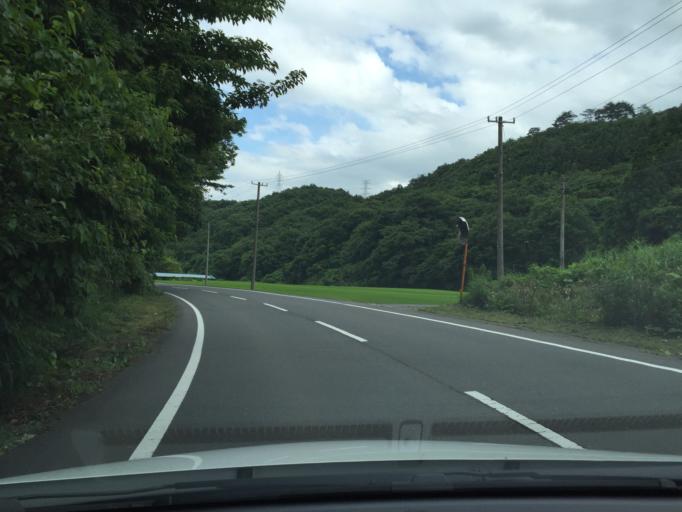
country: JP
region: Fukushima
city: Sukagawa
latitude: 37.1853
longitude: 140.2012
